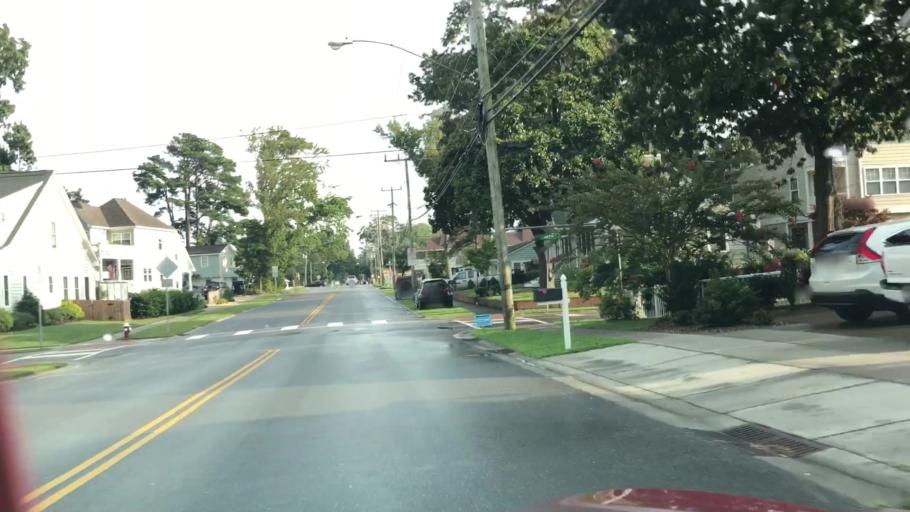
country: US
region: Virginia
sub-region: City of Virginia Beach
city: Virginia Beach
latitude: 36.8392
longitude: -75.9798
